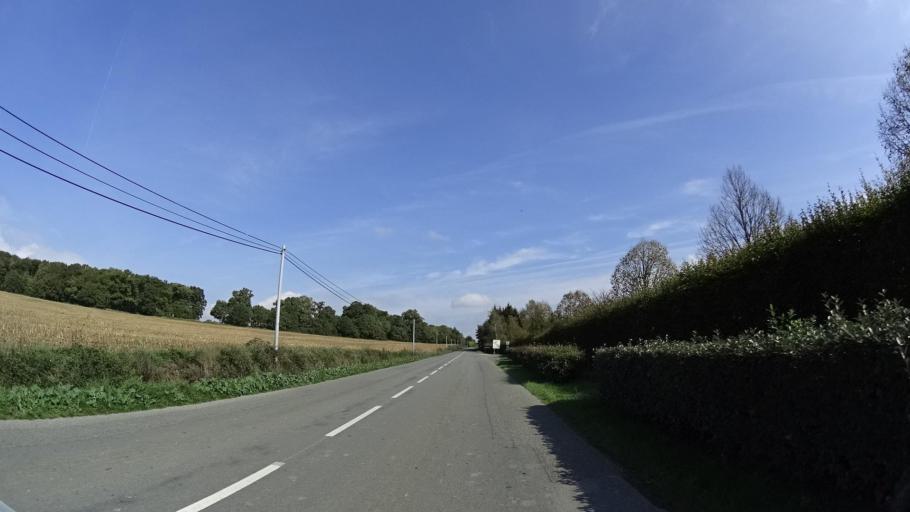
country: FR
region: Brittany
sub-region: Departement d'Ille-et-Vilaine
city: Medreac
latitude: 48.2701
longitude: -2.0553
